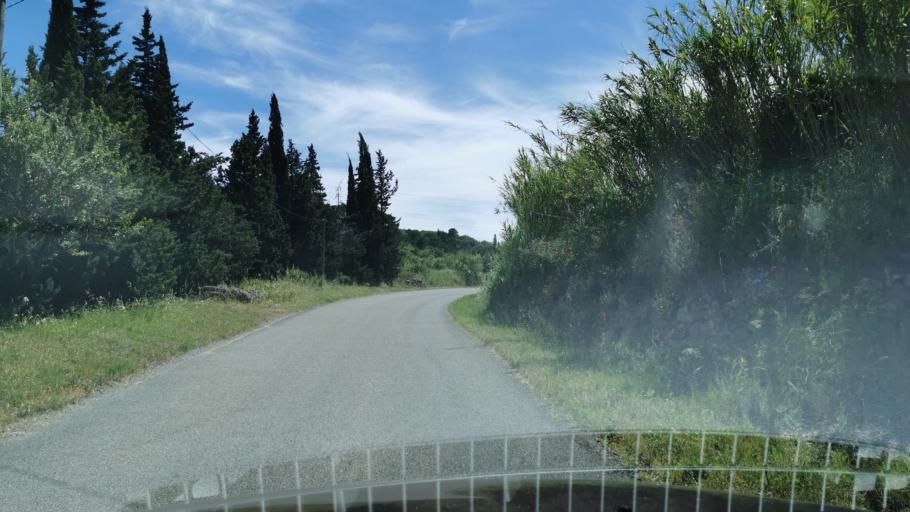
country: FR
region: Languedoc-Roussillon
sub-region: Departement de l'Aude
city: Nevian
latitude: 43.2028
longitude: 2.9034
